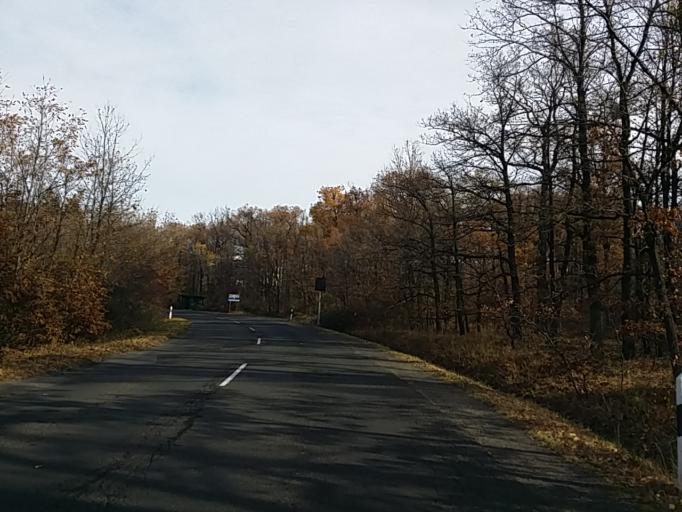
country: HU
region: Heves
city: Gyongyossolymos
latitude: 47.8530
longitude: 19.9703
